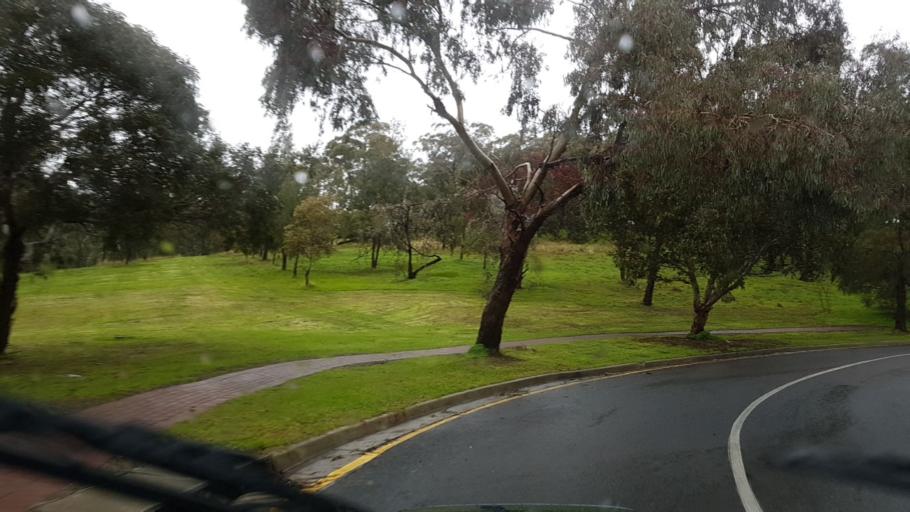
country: AU
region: South Australia
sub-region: Onkaparinga
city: Craigburn Farm
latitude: -35.0839
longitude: 138.5957
